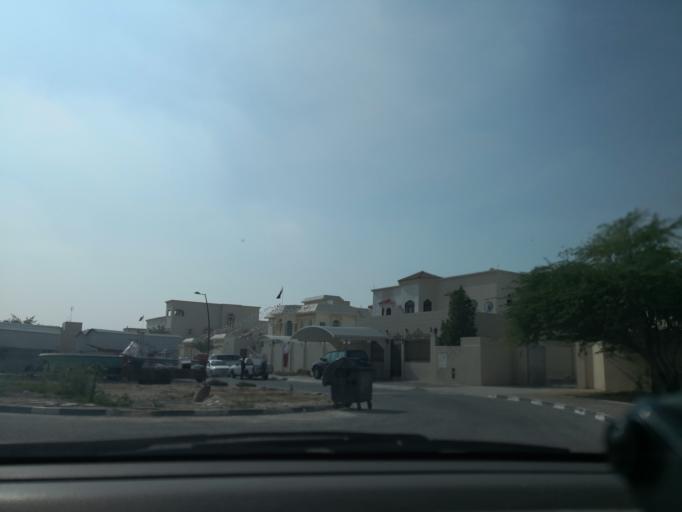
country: QA
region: Baladiyat ad Dawhah
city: Doha
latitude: 25.3473
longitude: 51.4900
